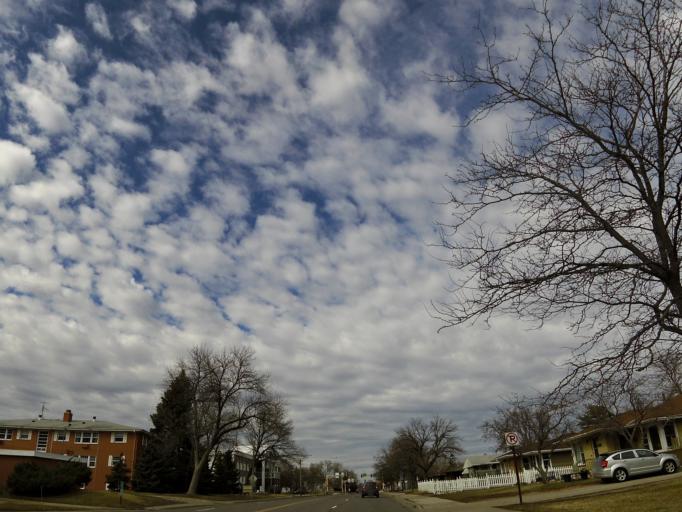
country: US
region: Minnesota
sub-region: Hennepin County
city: Edina
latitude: 44.8886
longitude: -93.3188
